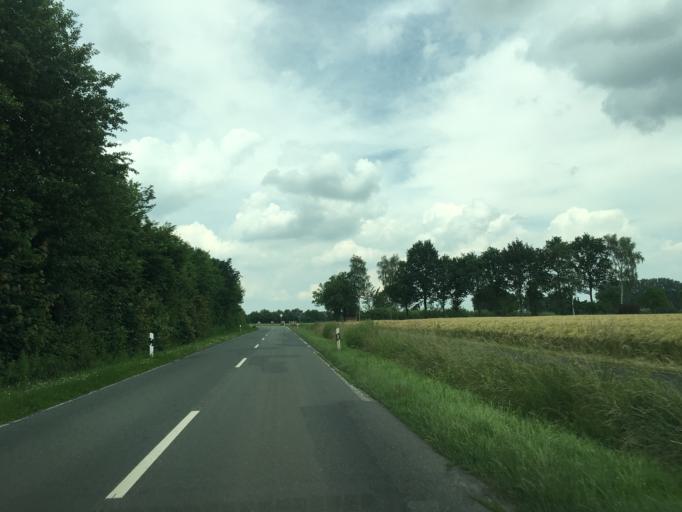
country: DE
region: North Rhine-Westphalia
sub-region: Regierungsbezirk Munster
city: Havixbeck
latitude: 52.0003
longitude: 7.3854
